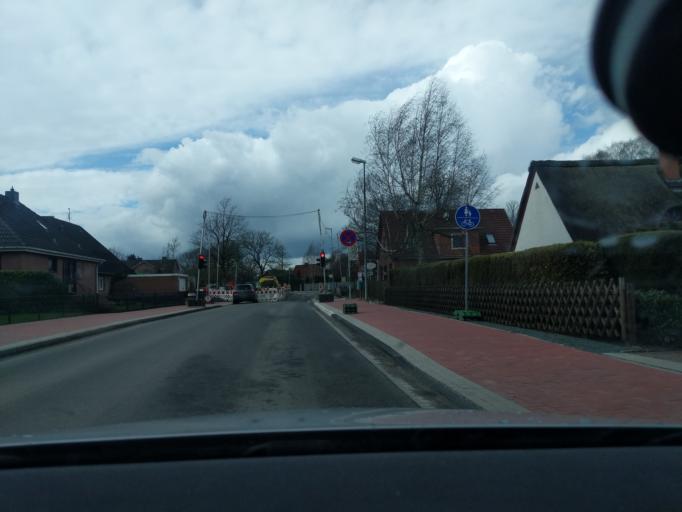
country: DE
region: Lower Saxony
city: Stade
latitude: 53.6171
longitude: 9.4623
